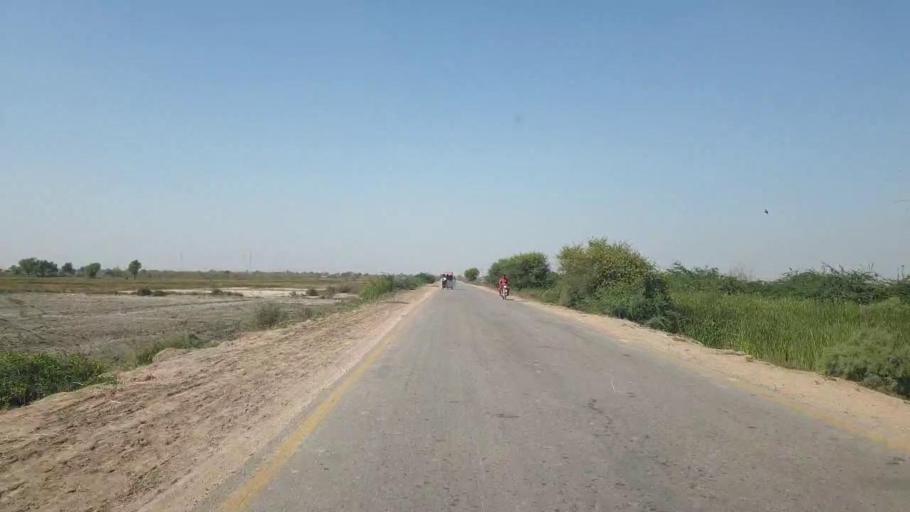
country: PK
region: Sindh
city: Rajo Khanani
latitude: 25.0507
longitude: 68.8079
